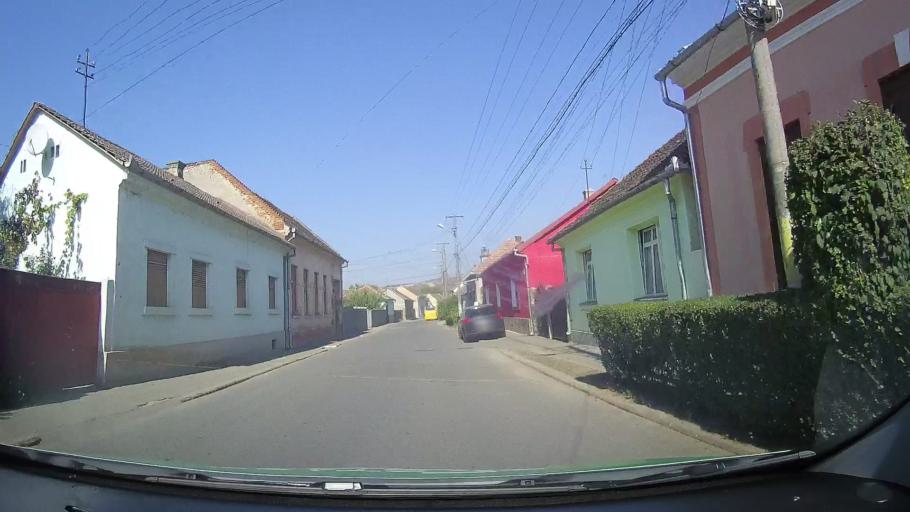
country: RO
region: Arad
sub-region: Oras Lipova
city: Lipova
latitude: 46.0881
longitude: 21.6910
